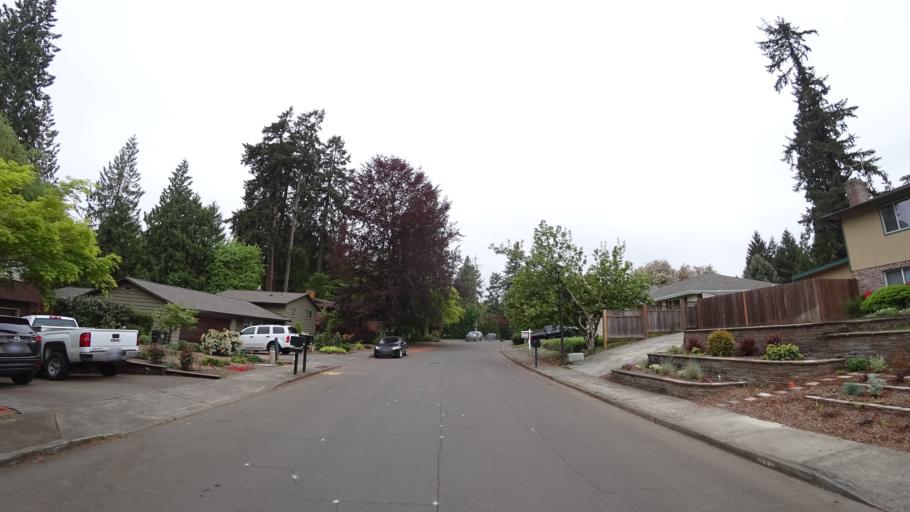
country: US
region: Oregon
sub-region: Washington County
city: Aloha
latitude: 45.5100
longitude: -122.8696
